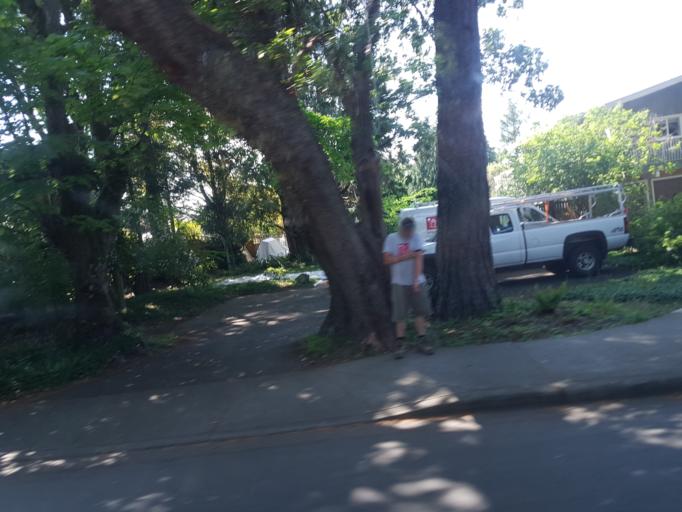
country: CA
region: British Columbia
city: Oak Bay
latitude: 48.4885
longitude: -123.3185
